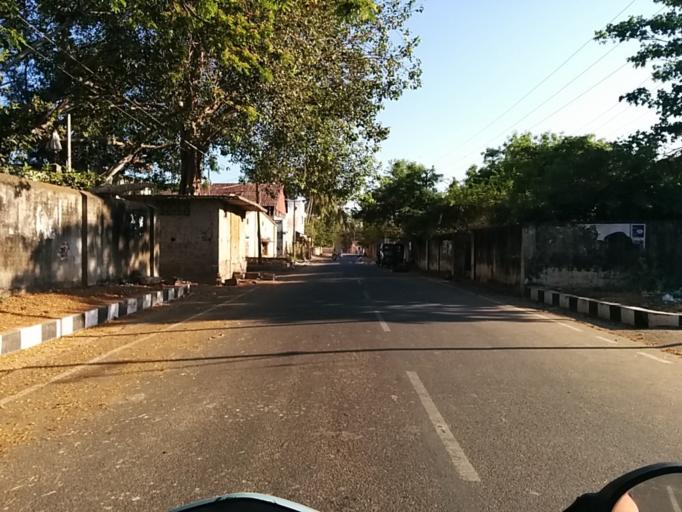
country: IN
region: Pondicherry
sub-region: Puducherry
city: Puducherry
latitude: 11.9201
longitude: 79.8301
